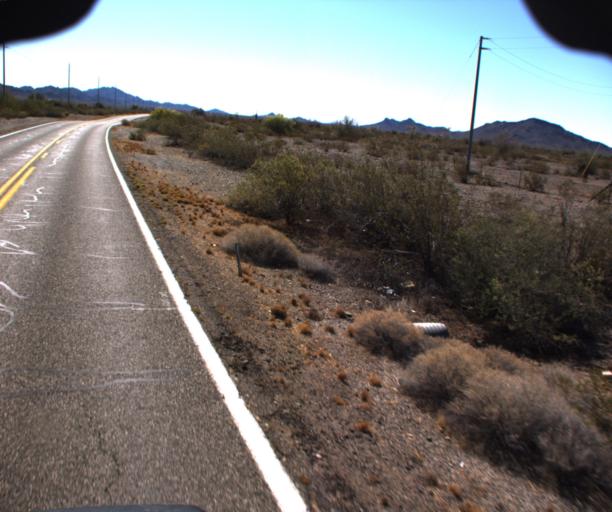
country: US
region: Arizona
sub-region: La Paz County
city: Salome
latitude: 33.7423
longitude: -113.7459
